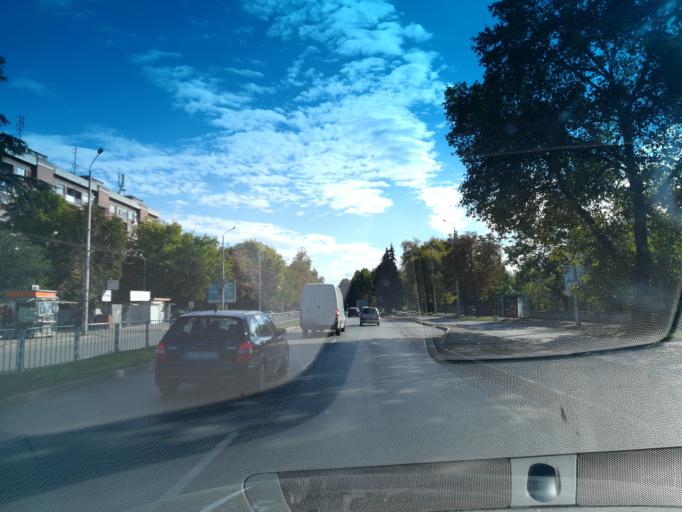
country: BG
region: Stara Zagora
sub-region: Obshtina Stara Zagora
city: Stara Zagora
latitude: 42.4090
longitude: 25.6400
